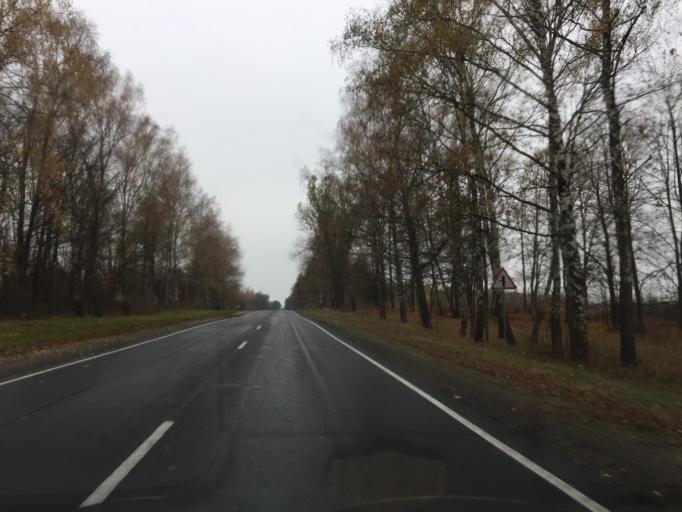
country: BY
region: Gomel
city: Karma
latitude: 53.3346
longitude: 30.7901
